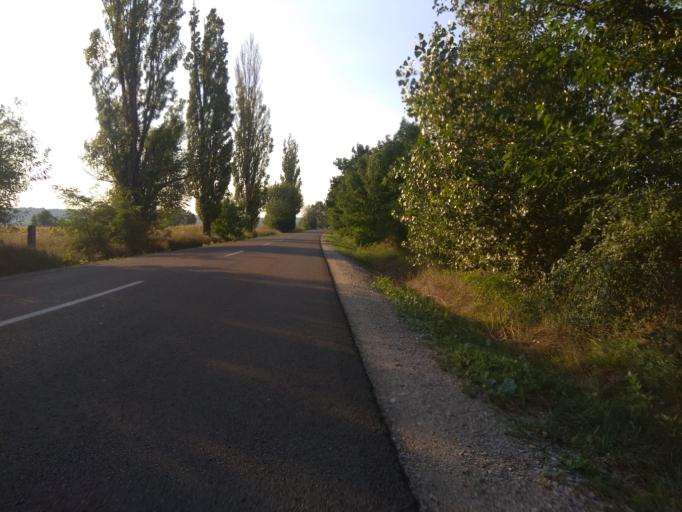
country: HU
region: Borsod-Abauj-Zemplen
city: Nyekladhaza
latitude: 47.9671
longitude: 20.8569
